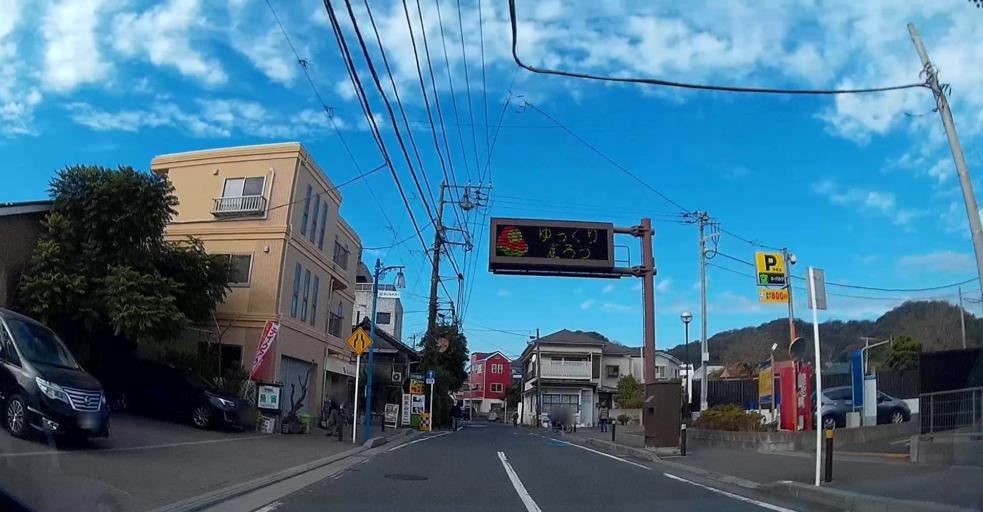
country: JP
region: Kanagawa
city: Hayama
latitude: 35.2759
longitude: 139.5730
